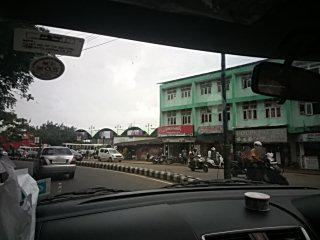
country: IN
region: Goa
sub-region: North Goa
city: Panaji
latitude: 15.4969
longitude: 73.8361
